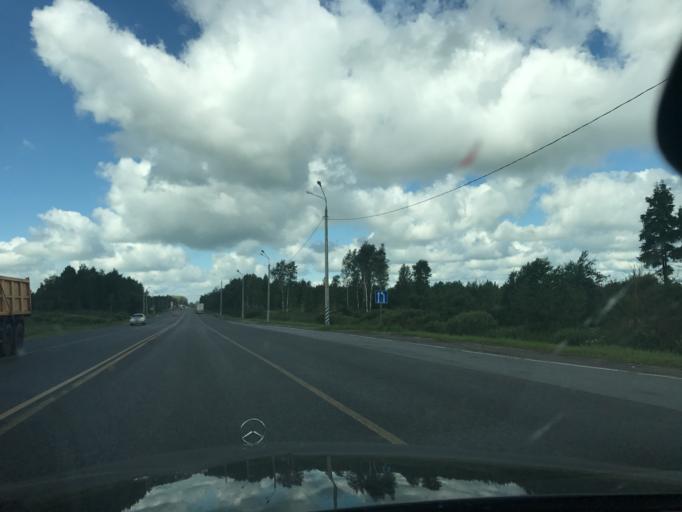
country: RU
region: Smolensk
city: Rudnya
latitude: 54.6922
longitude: 31.0861
